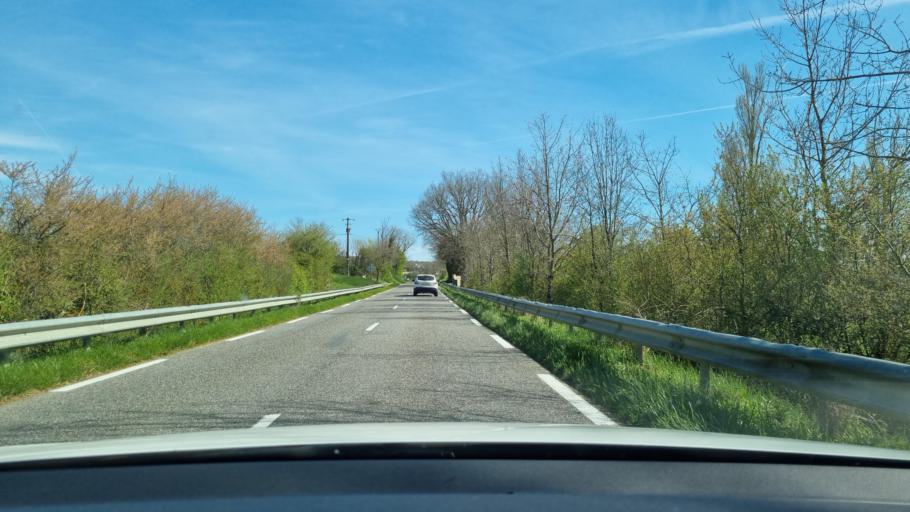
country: FR
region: Midi-Pyrenees
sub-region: Departement du Gers
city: Lombez
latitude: 43.4198
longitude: 0.8125
